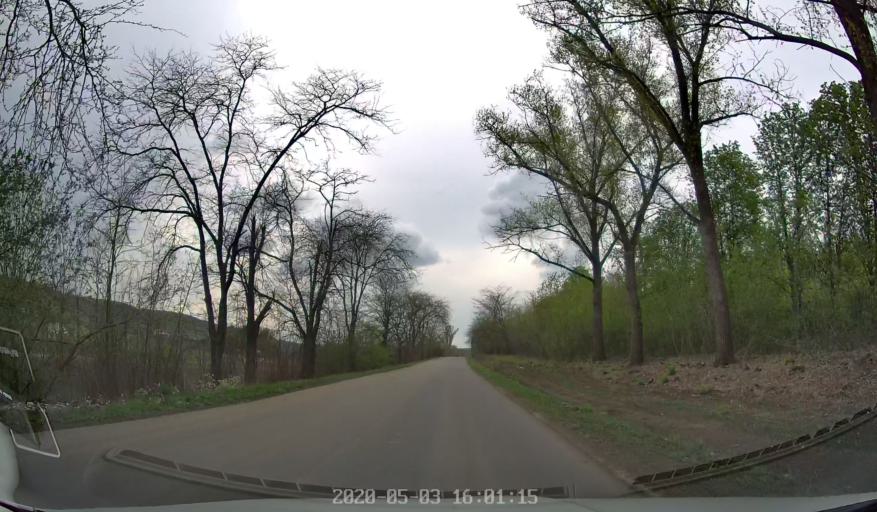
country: MD
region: Stinga Nistrului
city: Bucovat
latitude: 47.1648
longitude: 28.4112
